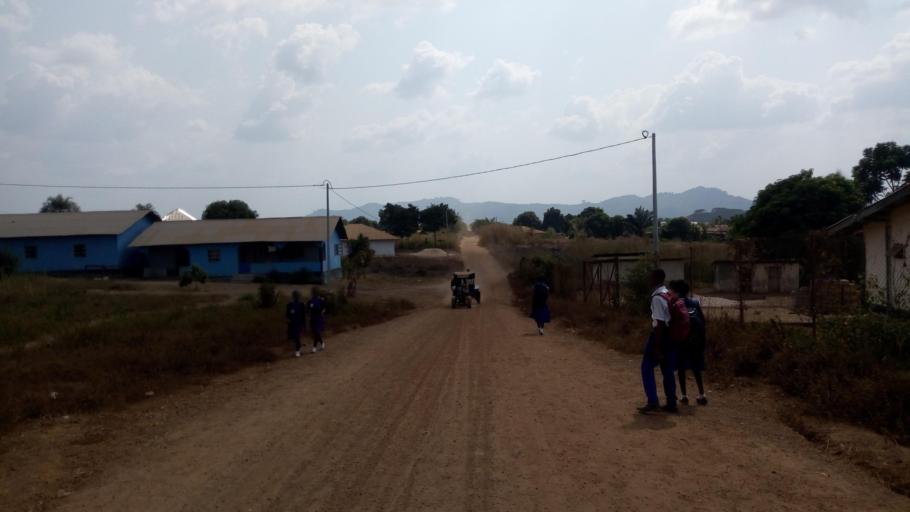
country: SL
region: Southern Province
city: Mogbwemo
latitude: 7.7787
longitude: -12.3008
